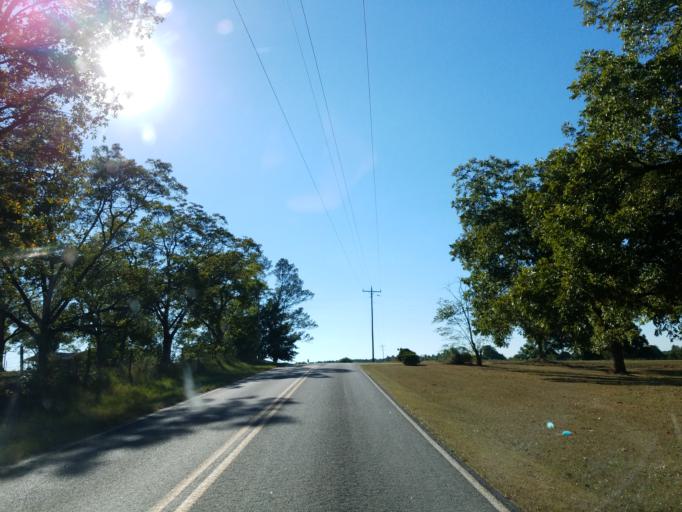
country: US
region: Georgia
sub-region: Dooly County
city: Unadilla
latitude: 32.2439
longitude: -83.8055
